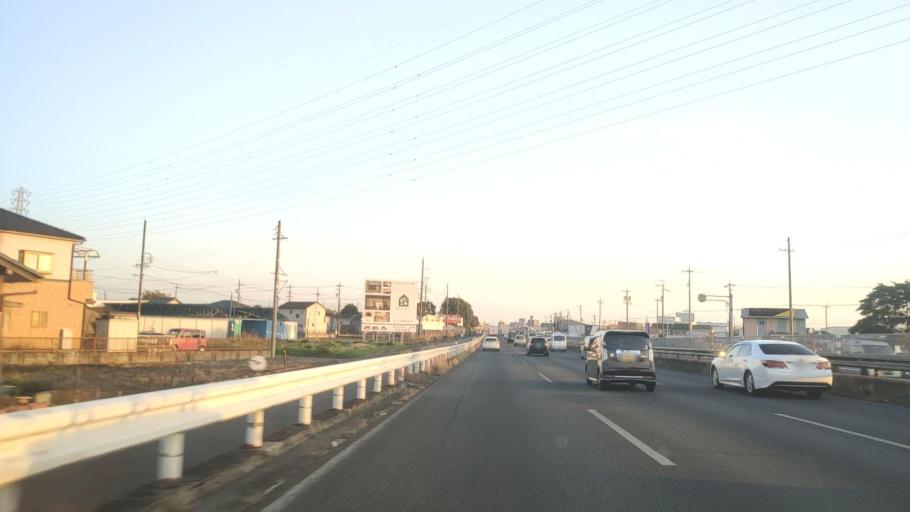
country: JP
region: Aichi
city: Kuroda
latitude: 35.3340
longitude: 136.8018
